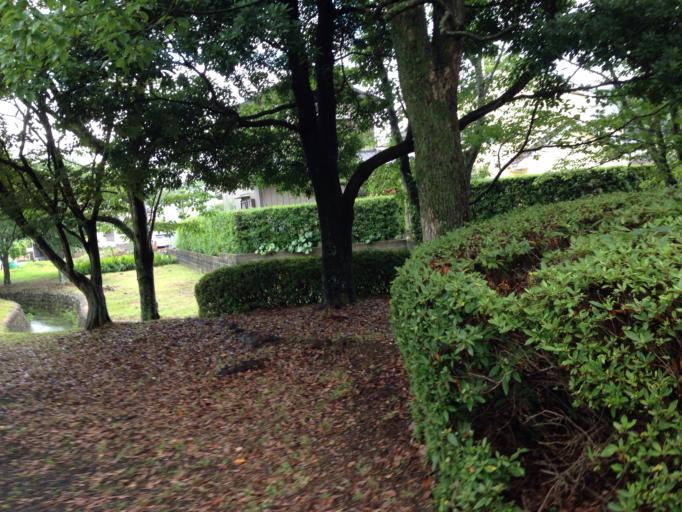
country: JP
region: Shizuoka
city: Fukuroi
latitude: 34.7440
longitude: 137.9461
